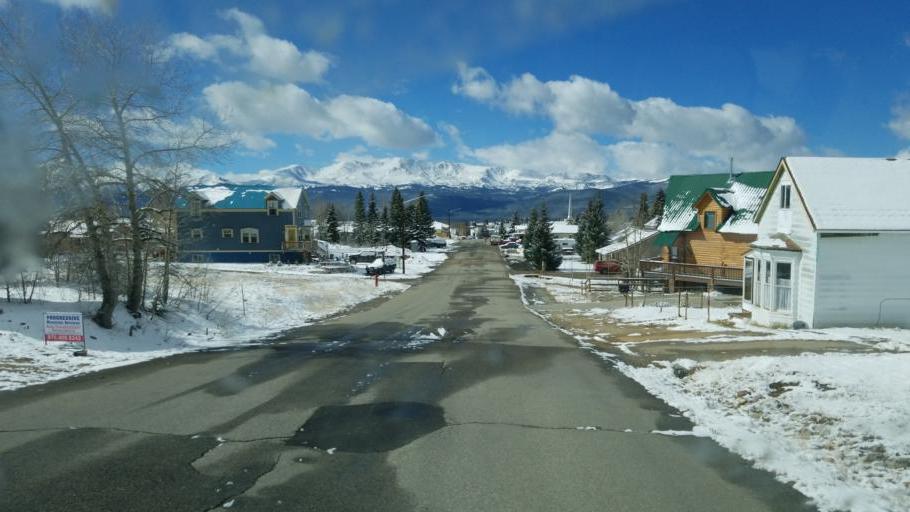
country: US
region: Colorado
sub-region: Lake County
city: Leadville
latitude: 39.2508
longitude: -106.2828
